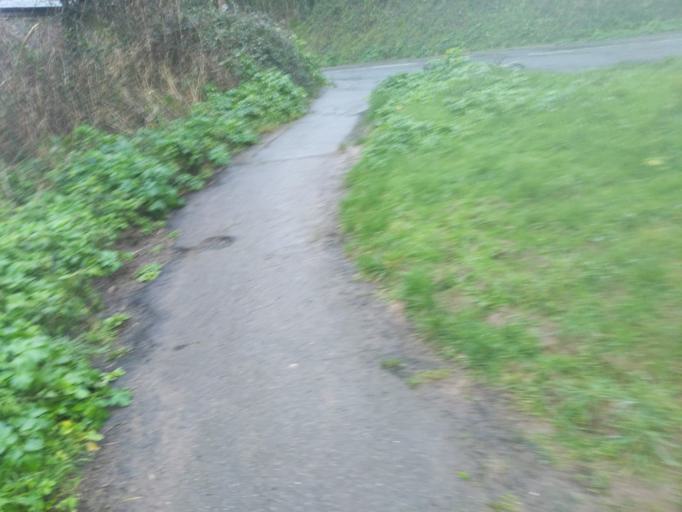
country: GB
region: England
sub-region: Cornwall
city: Millbrook
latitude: 50.3390
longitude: -4.2067
